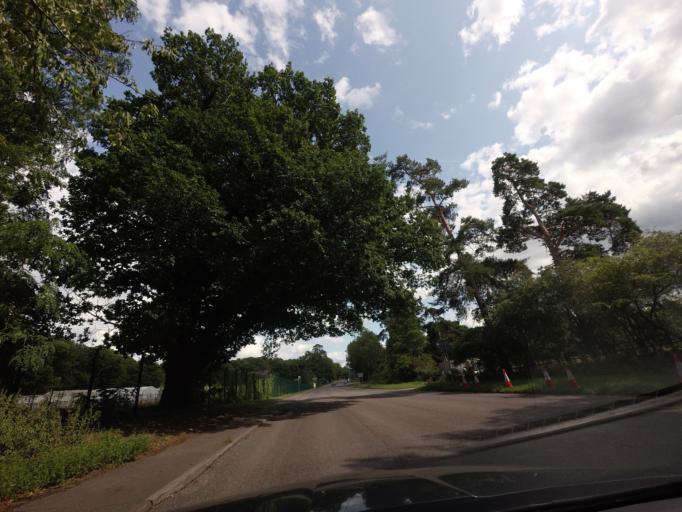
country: GB
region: England
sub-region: Kent
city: Boxley
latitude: 51.2673
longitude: 0.5920
